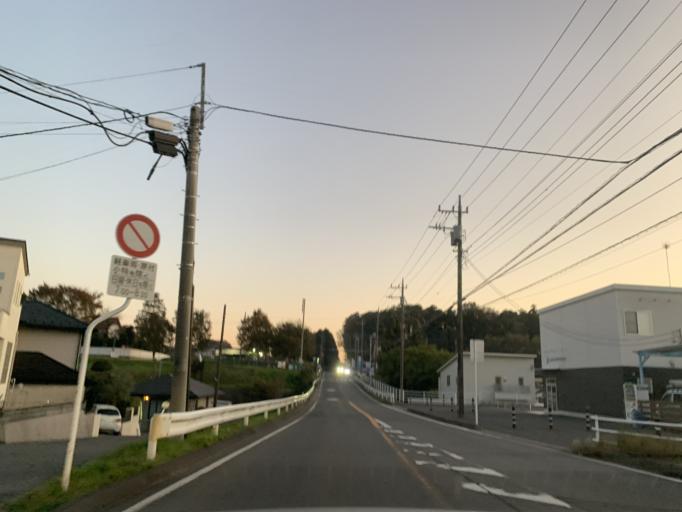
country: JP
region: Chiba
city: Nagareyama
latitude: 35.8908
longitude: 139.9010
